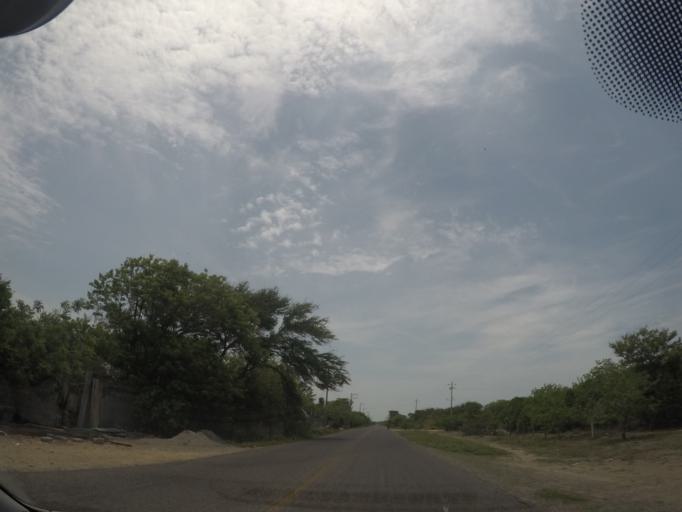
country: MX
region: Oaxaca
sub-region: San Mateo del Mar
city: Colonia Juarez
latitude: 16.2073
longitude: -95.0110
